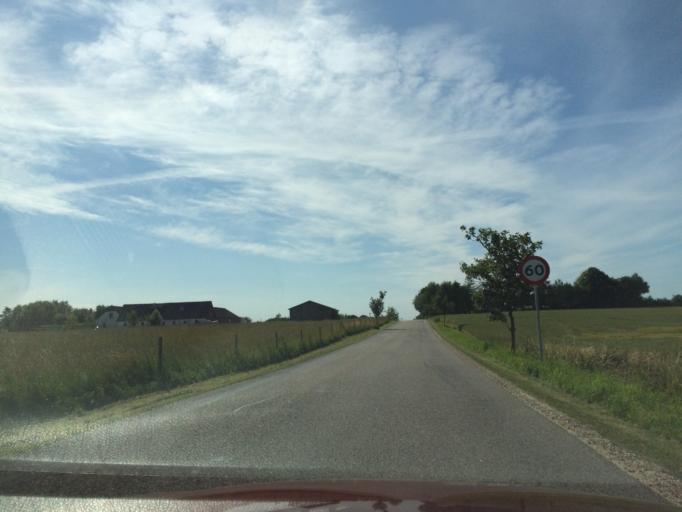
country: DK
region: Central Jutland
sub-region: Silkeborg Kommune
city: Svejbaek
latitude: 56.2251
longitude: 9.6251
